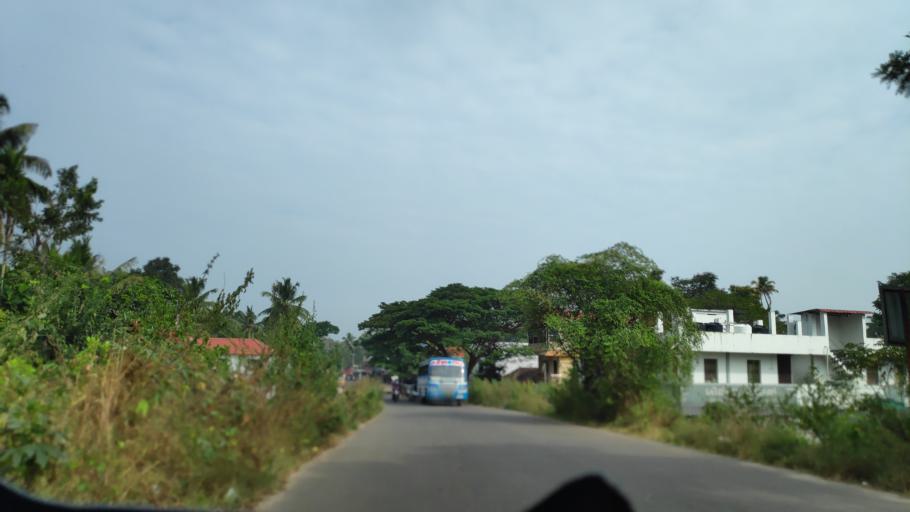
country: IN
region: Kerala
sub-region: Alappuzha
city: Kutiatodu
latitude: 9.7958
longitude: 76.3542
